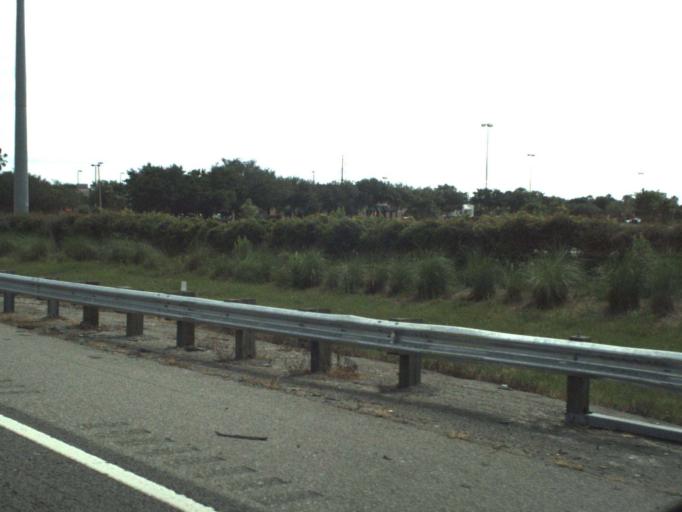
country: US
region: Florida
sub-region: Seminole County
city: Lake Mary
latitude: 28.8066
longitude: -81.3401
